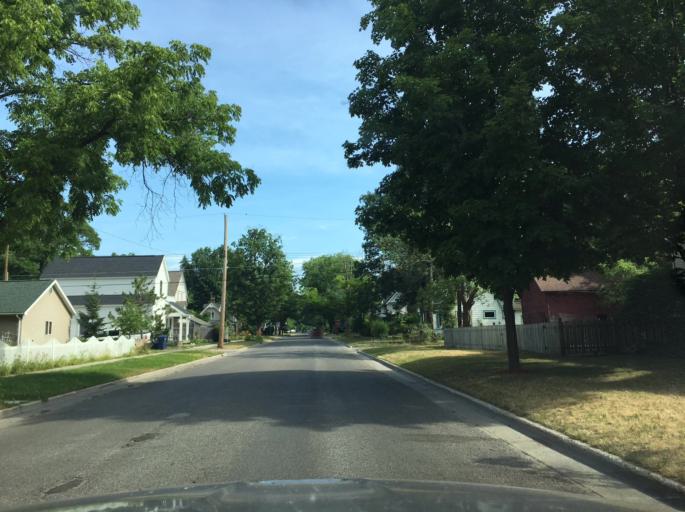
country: US
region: Michigan
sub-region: Grand Traverse County
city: Traverse City
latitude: 44.7583
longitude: -85.6329
